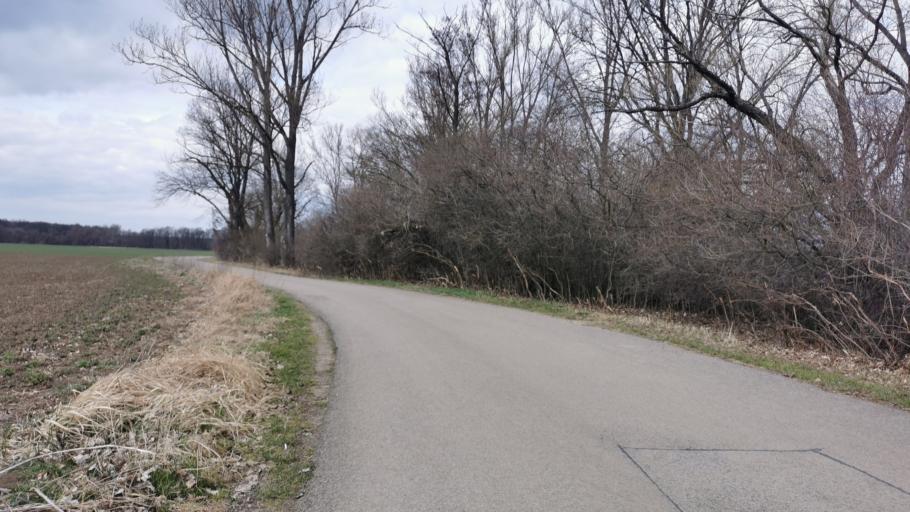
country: SK
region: Trnavsky
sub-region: Okres Skalica
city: Skalica
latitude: 48.8673
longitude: 17.2160
